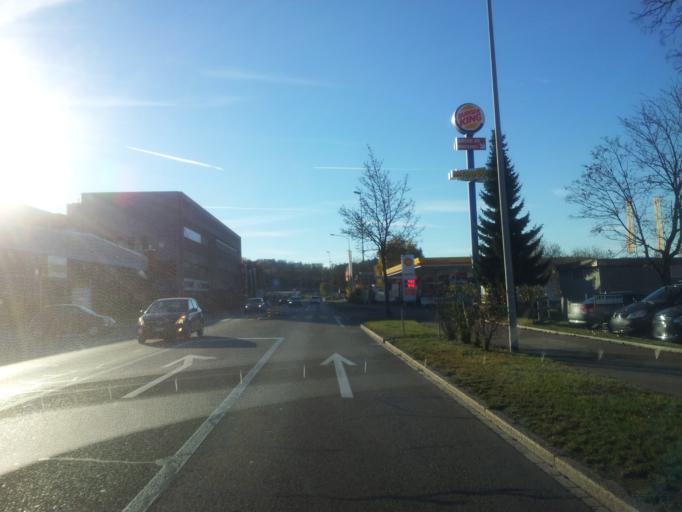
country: CH
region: Zurich
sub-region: Bezirk Dielsdorf
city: Rumlang
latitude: 47.4613
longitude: 8.5256
